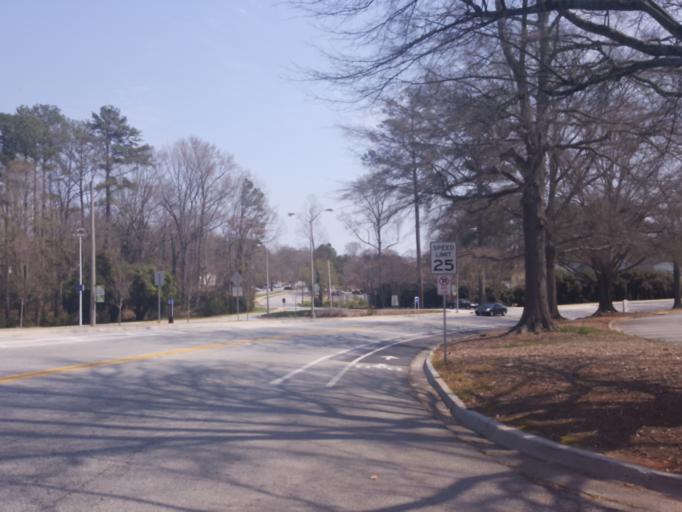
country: US
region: Georgia
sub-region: Carroll County
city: Carrollton
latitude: 33.5754
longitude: -85.0952
